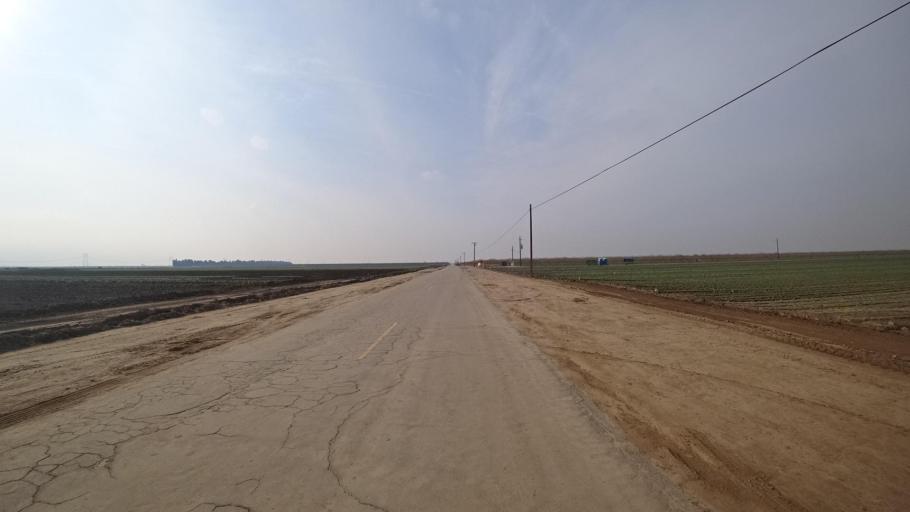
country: US
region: California
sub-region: Kern County
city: Weedpatch
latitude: 35.1366
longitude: -118.9486
